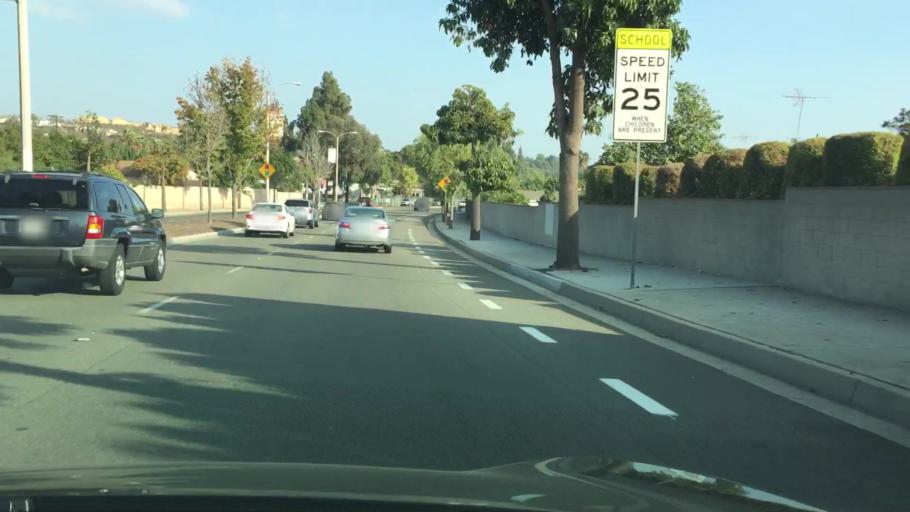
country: US
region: California
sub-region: Los Angeles County
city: East La Mirada
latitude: 33.8984
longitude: -117.9925
